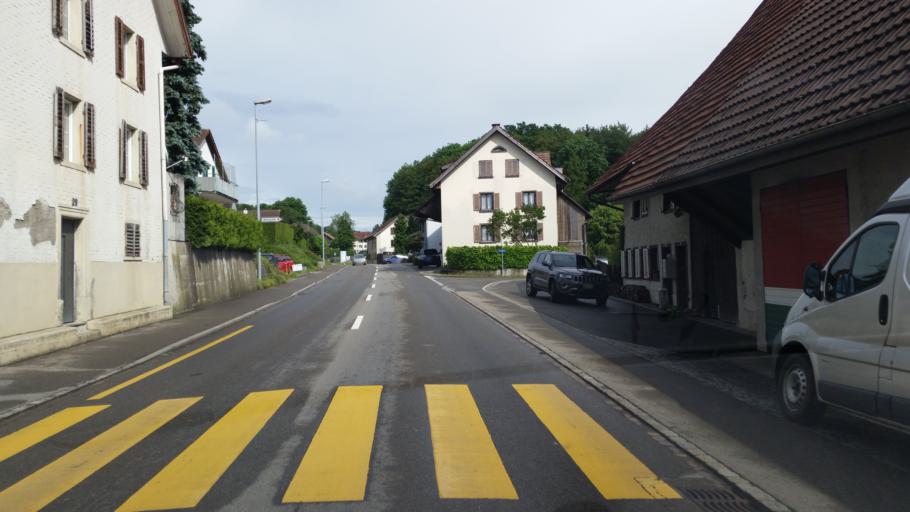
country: CH
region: Aargau
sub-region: Bezirk Muri
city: Waltenschwil
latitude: 47.3347
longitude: 8.3052
